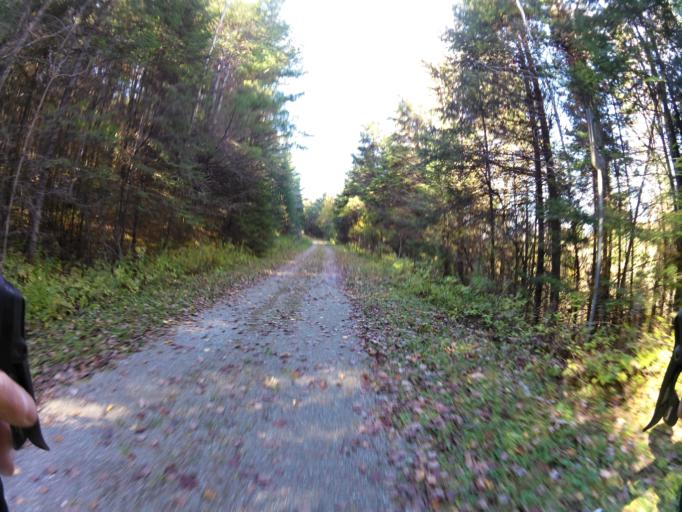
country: CA
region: Quebec
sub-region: Outaouais
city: Wakefield
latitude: 45.8581
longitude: -75.9936
